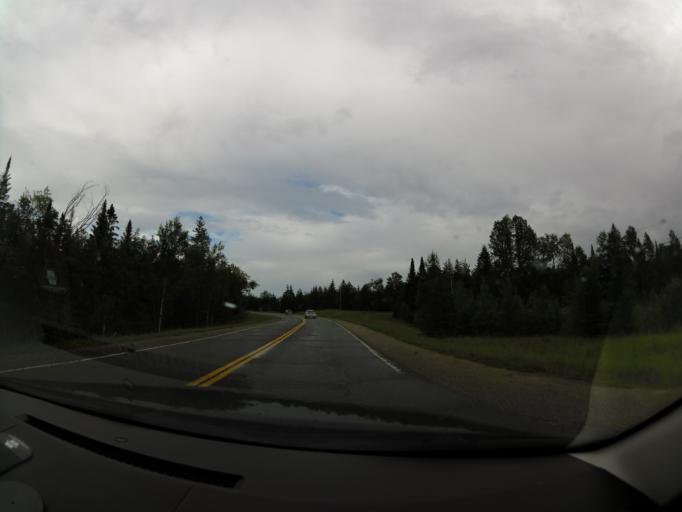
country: CA
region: Ontario
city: Carleton Place
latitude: 45.1116
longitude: -76.3658
